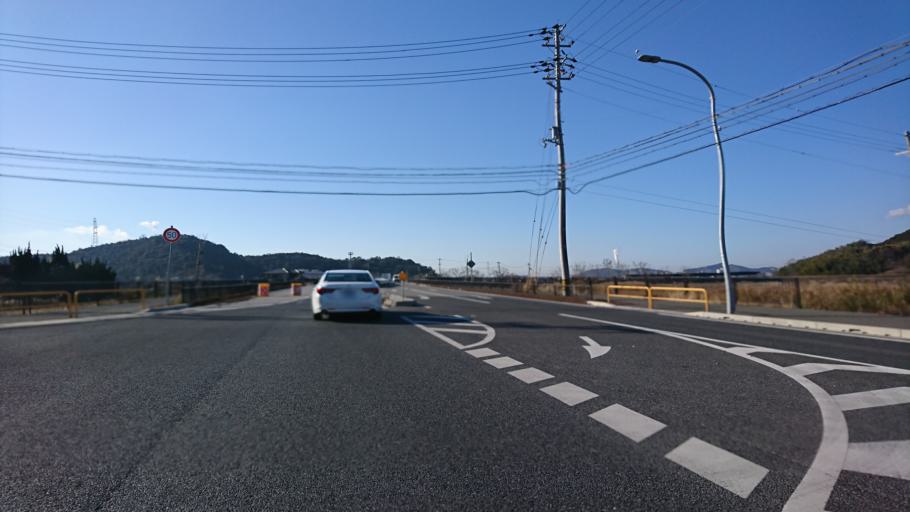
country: JP
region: Hyogo
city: Kakogawacho-honmachi
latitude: 34.8080
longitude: 134.8355
